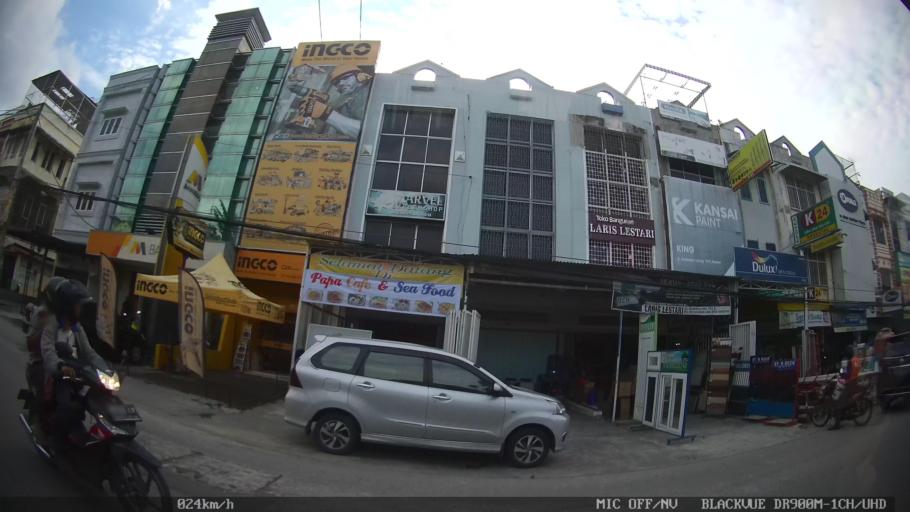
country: ID
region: North Sumatra
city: Medan
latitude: 3.6211
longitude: 98.6801
